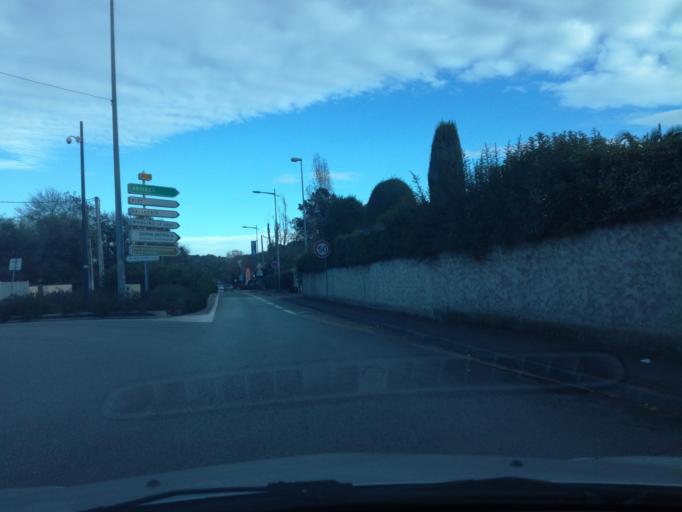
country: FR
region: Provence-Alpes-Cote d'Azur
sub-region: Departement des Alpes-Maritimes
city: Mougins
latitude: 43.6021
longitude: 7.0144
